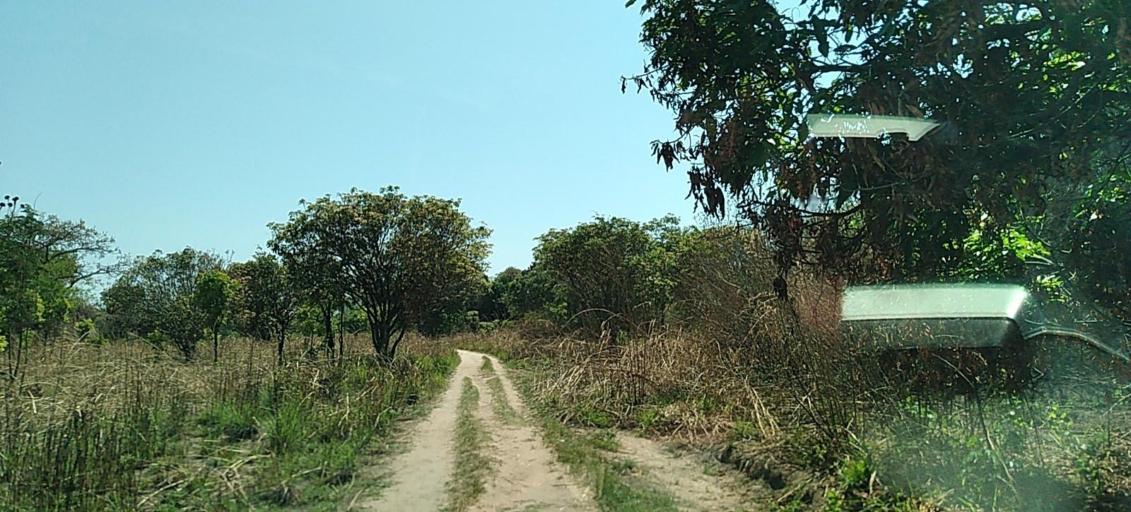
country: ZM
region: Copperbelt
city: Chililabombwe
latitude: -12.2863
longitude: 27.8809
